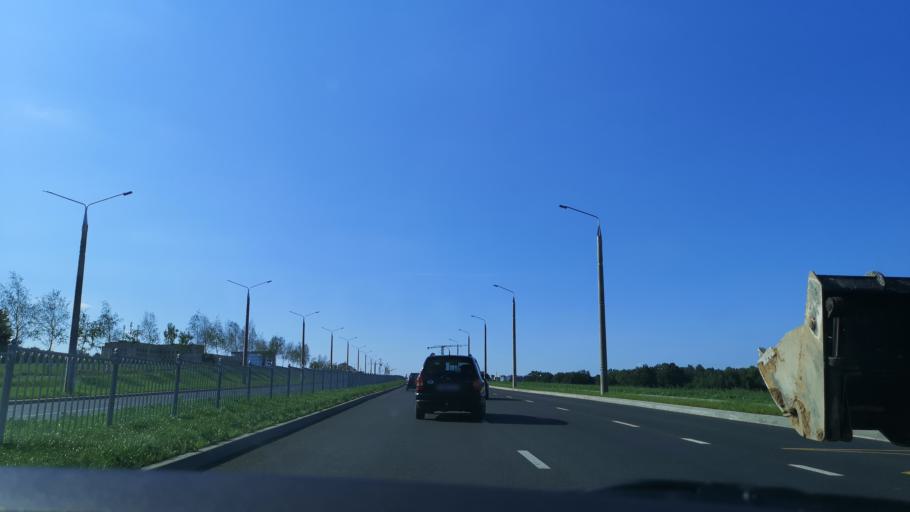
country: BY
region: Grodnenskaya
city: Hrodna
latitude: 53.6476
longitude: 23.8657
